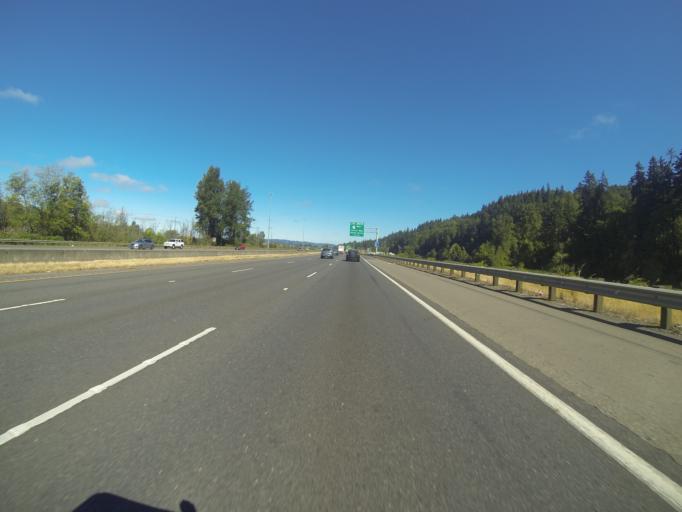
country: US
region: Washington
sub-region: Cowlitz County
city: Kelso
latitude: 46.0966
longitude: -122.8732
